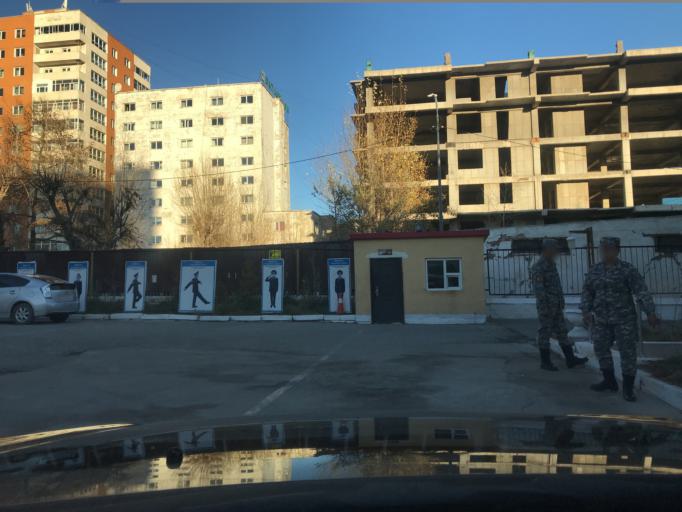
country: MN
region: Ulaanbaatar
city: Ulaanbaatar
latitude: 47.9228
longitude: 106.9085
